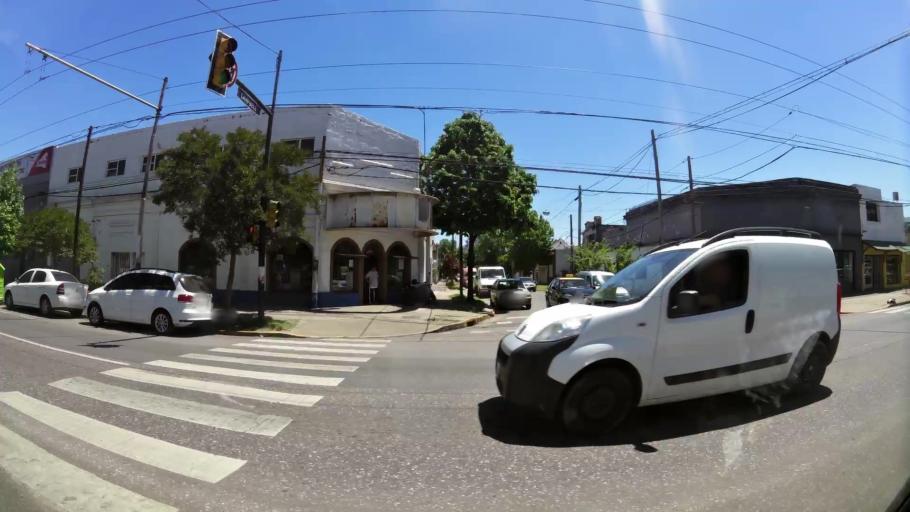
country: AR
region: Santa Fe
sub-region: Departamento de Rosario
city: Rosario
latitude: -32.9396
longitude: -60.7077
